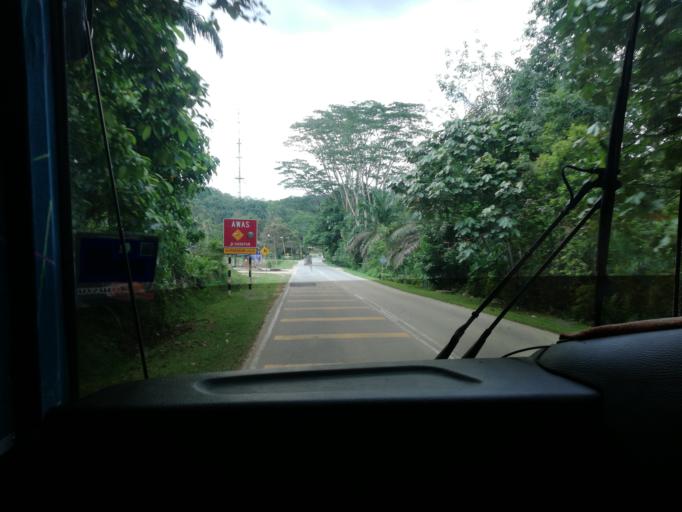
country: MY
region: Kedah
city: Kulim
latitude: 5.3309
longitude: 100.5890
